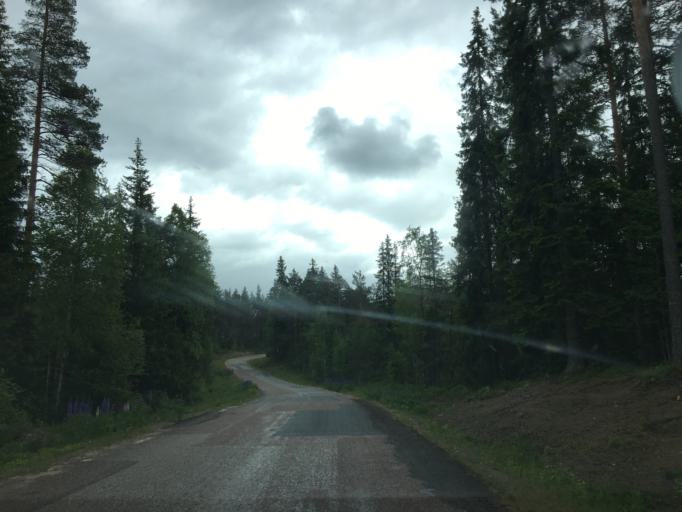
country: SE
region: OErebro
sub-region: Hallefors Kommun
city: Haellefors
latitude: 60.0918
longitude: 14.4778
